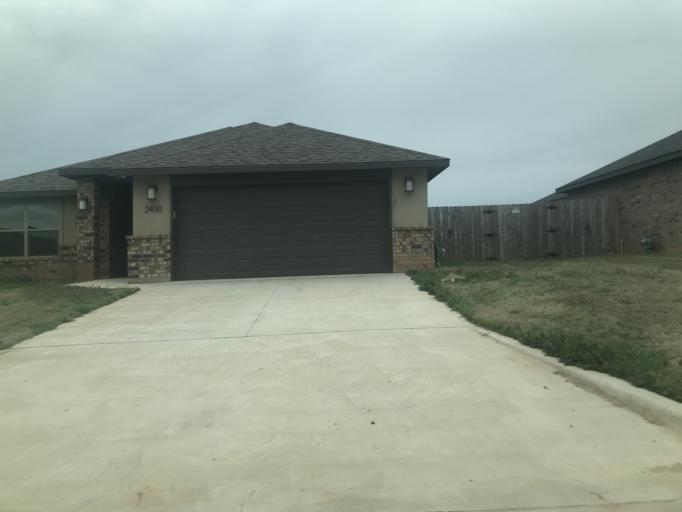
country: US
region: Texas
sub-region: Taylor County
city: Abilene
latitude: 32.4897
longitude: -99.6831
